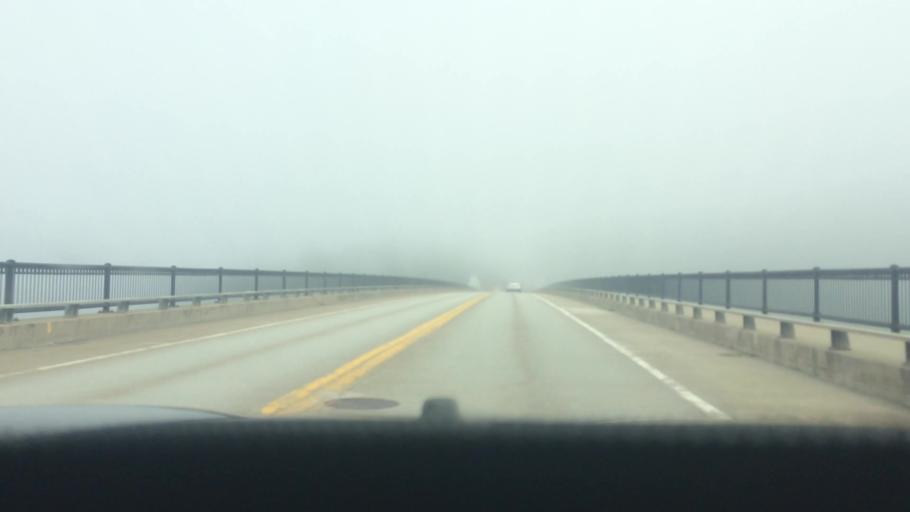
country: US
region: Massachusetts
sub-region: Franklin County
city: Millers Falls
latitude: 42.5972
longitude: -72.4955
